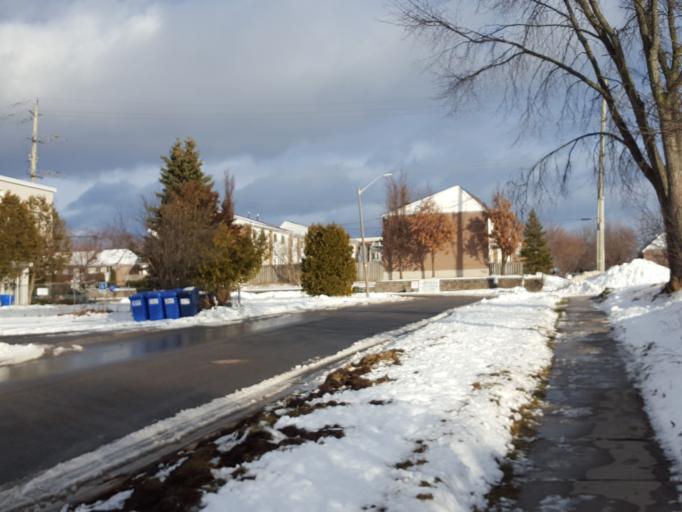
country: CA
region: Ontario
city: Kingston
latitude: 44.2378
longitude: -76.5328
